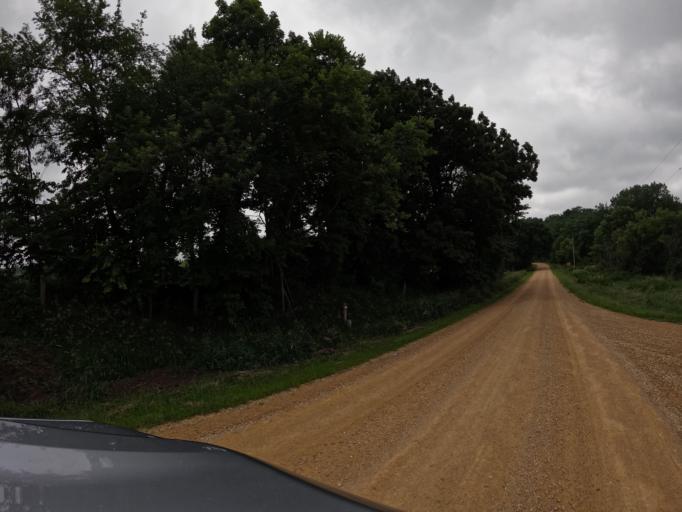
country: US
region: Illinois
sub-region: Carroll County
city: Savanna
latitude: 41.9967
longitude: -90.1795
